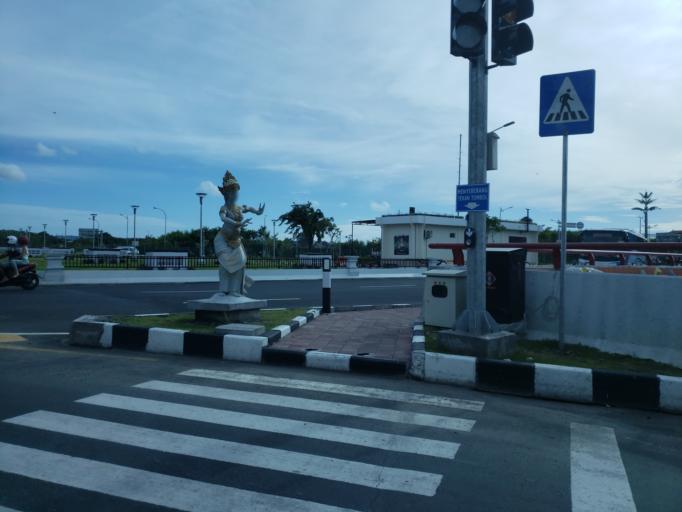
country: ID
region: Bali
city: Kelanabian
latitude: -8.7444
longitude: 115.1829
